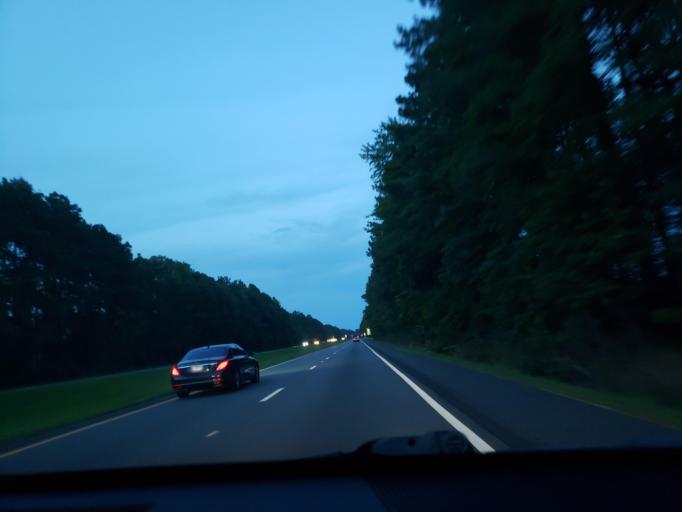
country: US
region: Virginia
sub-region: City of Franklin
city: Franklin
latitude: 36.6430
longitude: -76.8834
